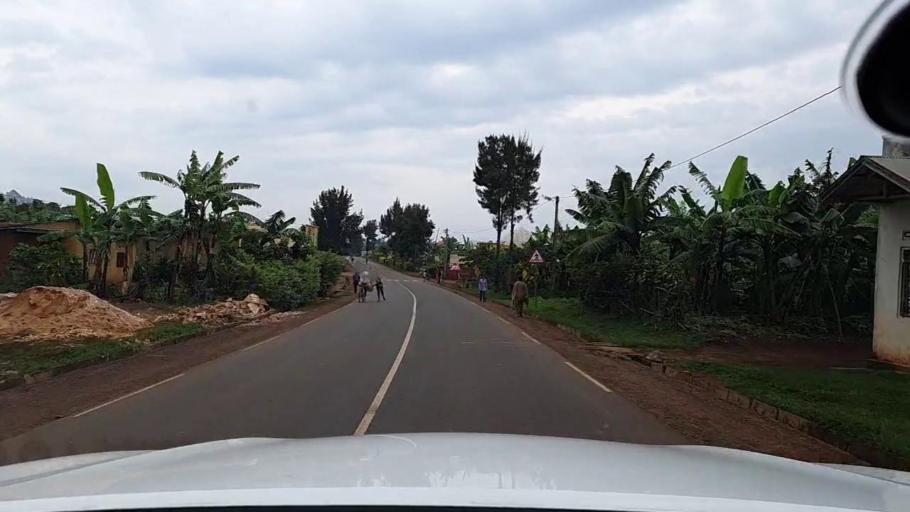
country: RW
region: Western Province
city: Cyangugu
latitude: -2.6038
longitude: 28.9333
